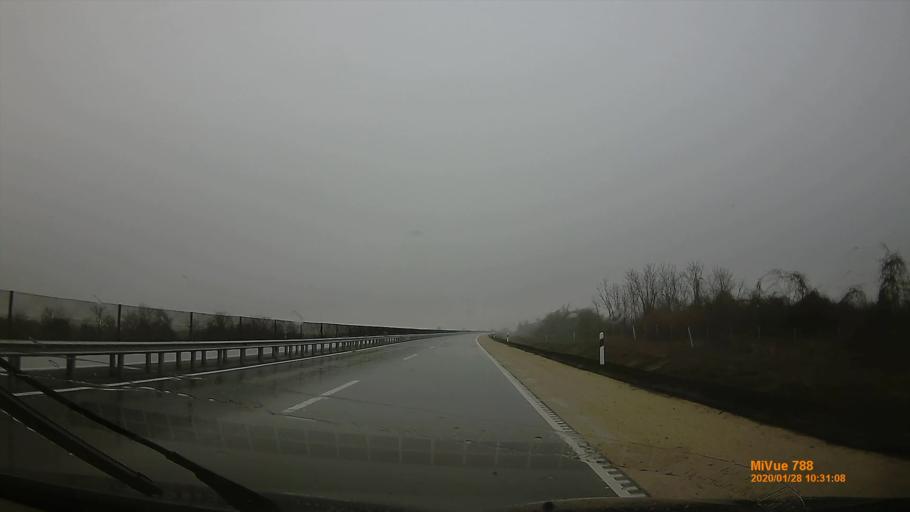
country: HU
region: Pest
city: Gomba
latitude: 47.3368
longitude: 19.5082
